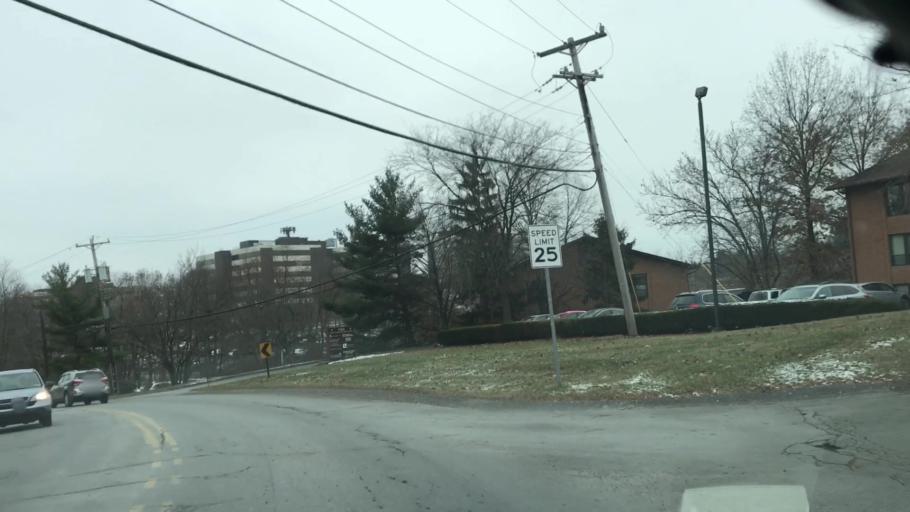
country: US
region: Pennsylvania
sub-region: Allegheny County
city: Carnot-Moon
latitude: 40.5042
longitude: -80.2093
